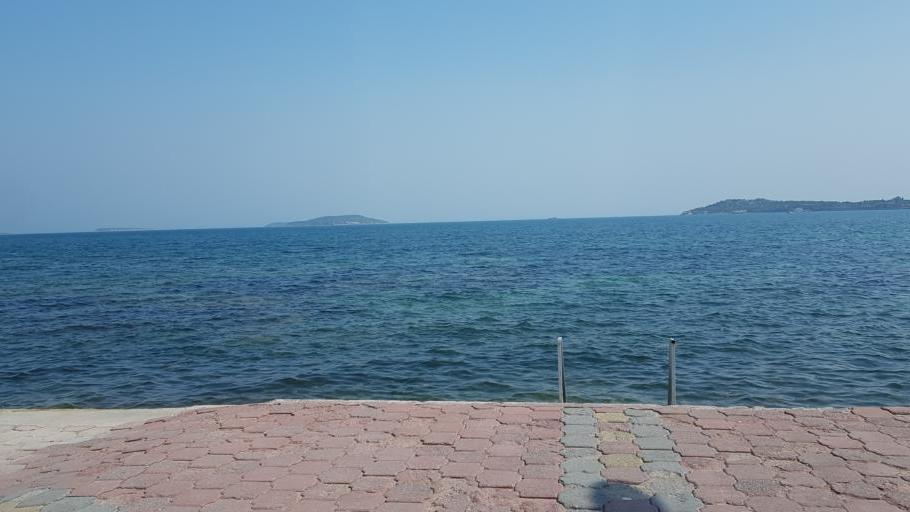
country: TR
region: Izmir
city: Urla
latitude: 38.3668
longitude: 26.7660
